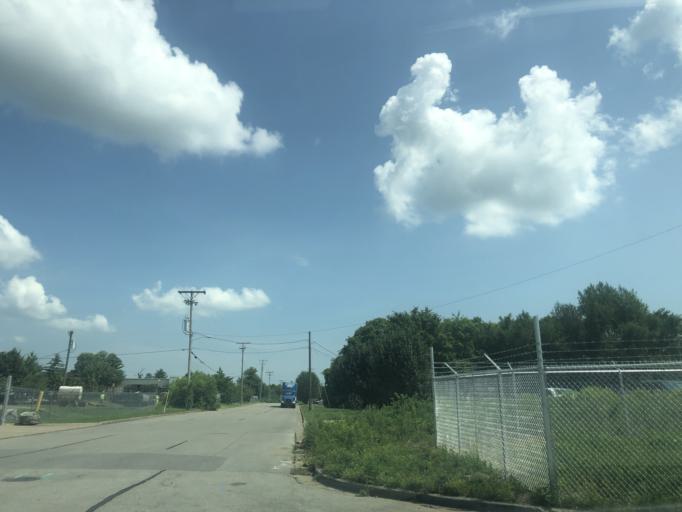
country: US
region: Tennessee
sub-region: Rutherford County
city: La Vergne
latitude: 36.0245
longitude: -86.5964
